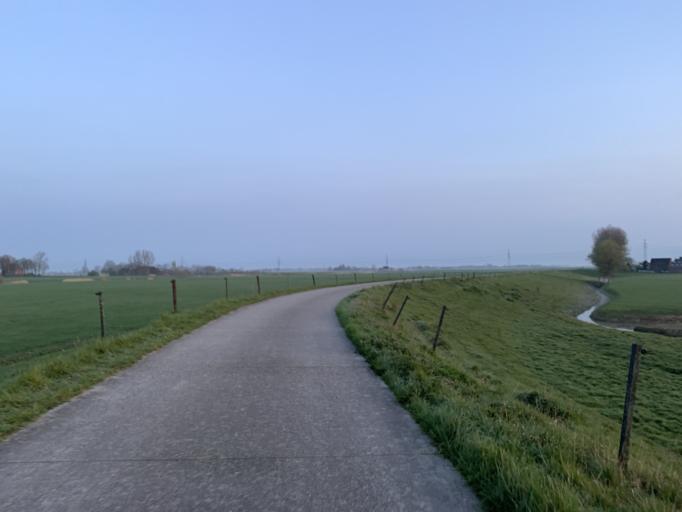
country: NL
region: Groningen
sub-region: Gemeente Zuidhorn
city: Aduard
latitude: 53.2784
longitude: 6.5058
